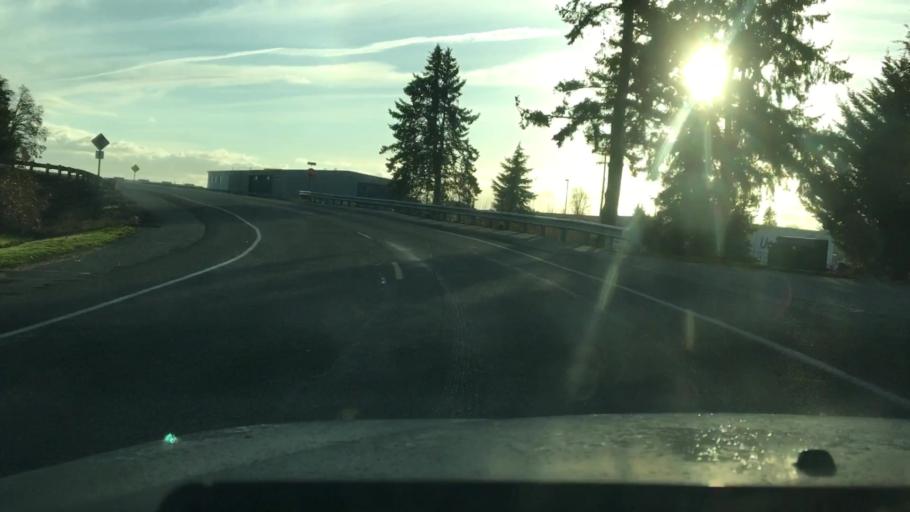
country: US
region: Washington
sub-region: Skagit County
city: Mount Vernon
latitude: 48.4002
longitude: -122.3328
